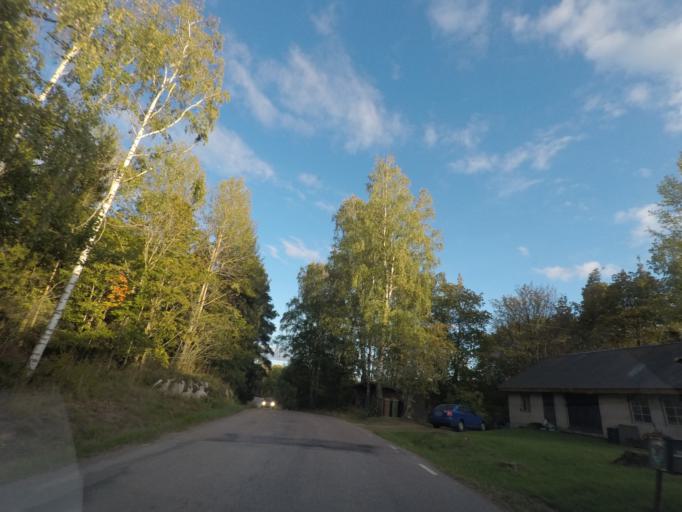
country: SE
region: Vaestmanland
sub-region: Kopings Kommun
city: Koping
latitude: 59.5101
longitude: 16.0639
